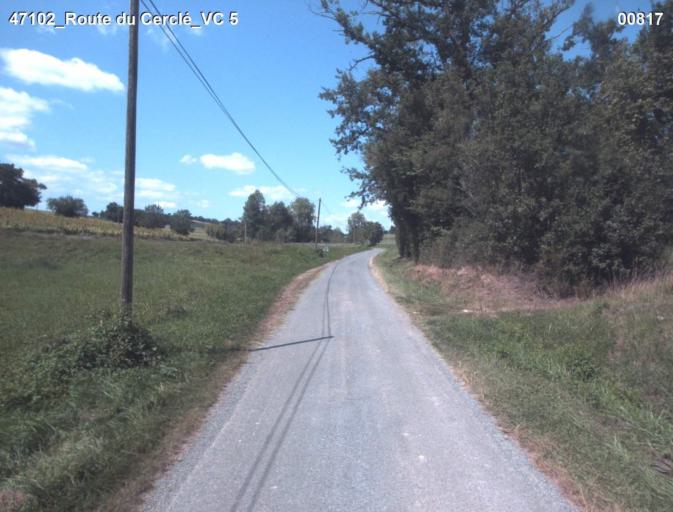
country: FR
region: Aquitaine
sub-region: Departement du Lot-et-Garonne
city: Laplume
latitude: 44.0747
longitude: 0.4529
